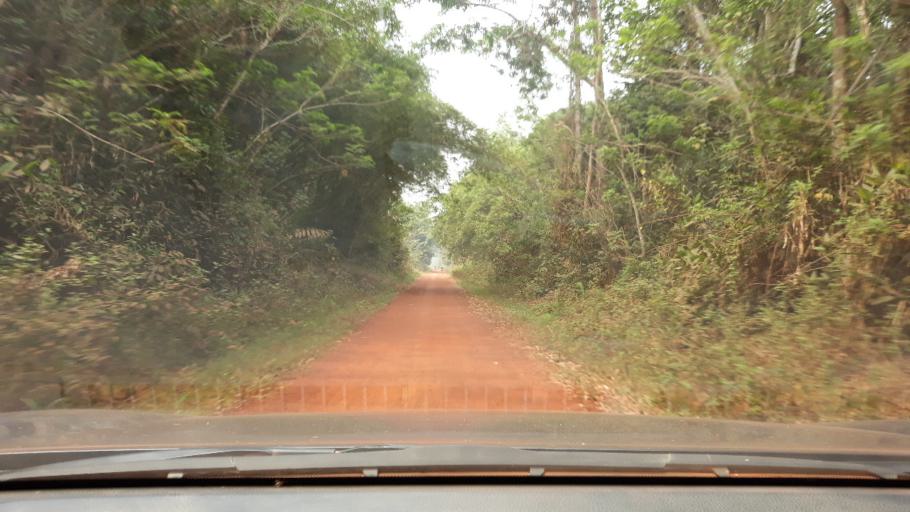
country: CD
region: Eastern Province
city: Aketi
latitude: 2.9348
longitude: 24.0958
